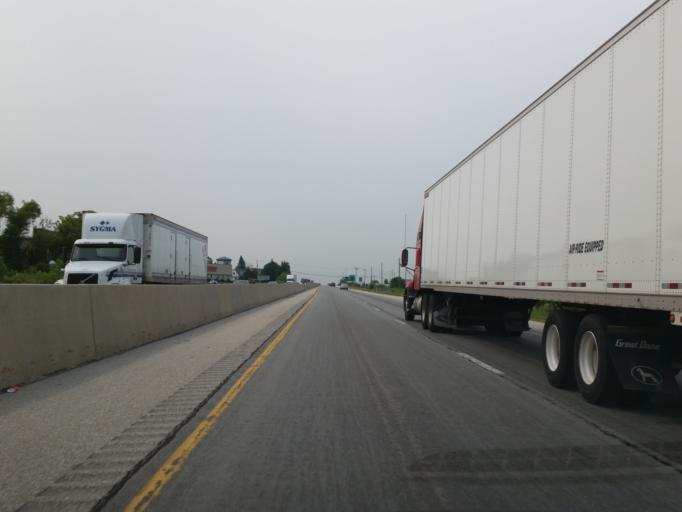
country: US
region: Pennsylvania
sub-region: York County
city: Emigsville
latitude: 40.0319
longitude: -76.7461
